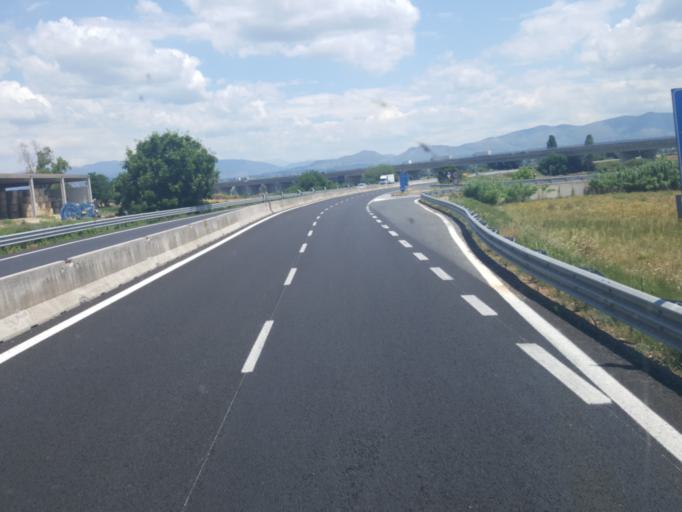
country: IT
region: Latium
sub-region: Citta metropolitana di Roma Capitale
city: Fiano Romano
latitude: 42.1477
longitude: 12.6201
